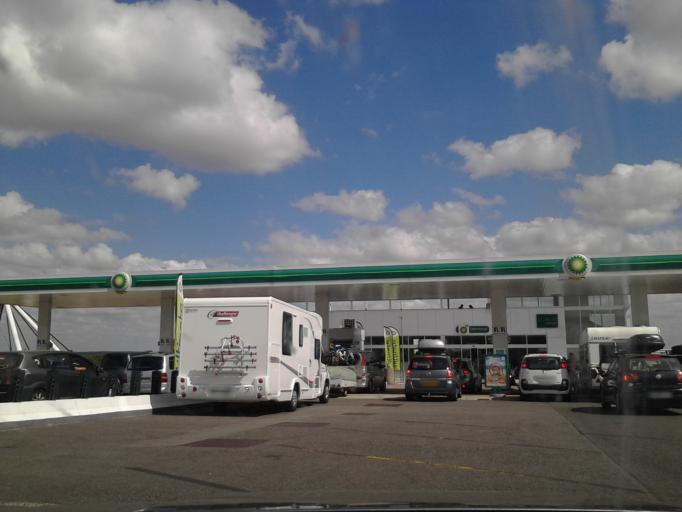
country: FR
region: Centre
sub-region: Departement du Cher
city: Orval
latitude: 46.7524
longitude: 2.4152
